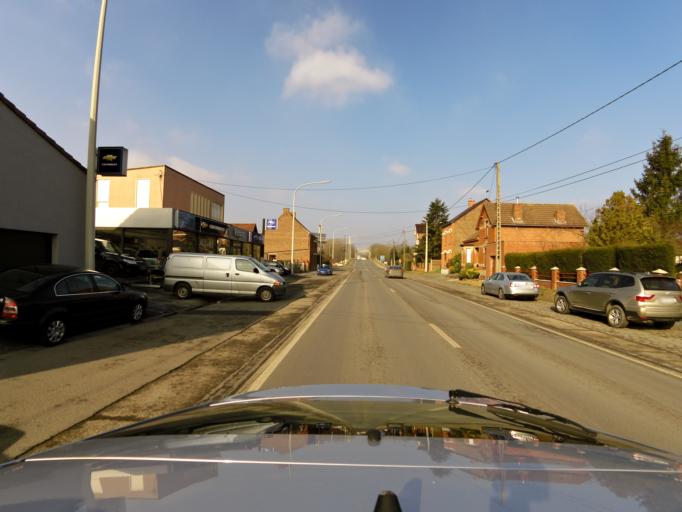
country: BE
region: Wallonia
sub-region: Province du Hainaut
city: Quaregnon
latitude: 50.4769
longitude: 3.8892
